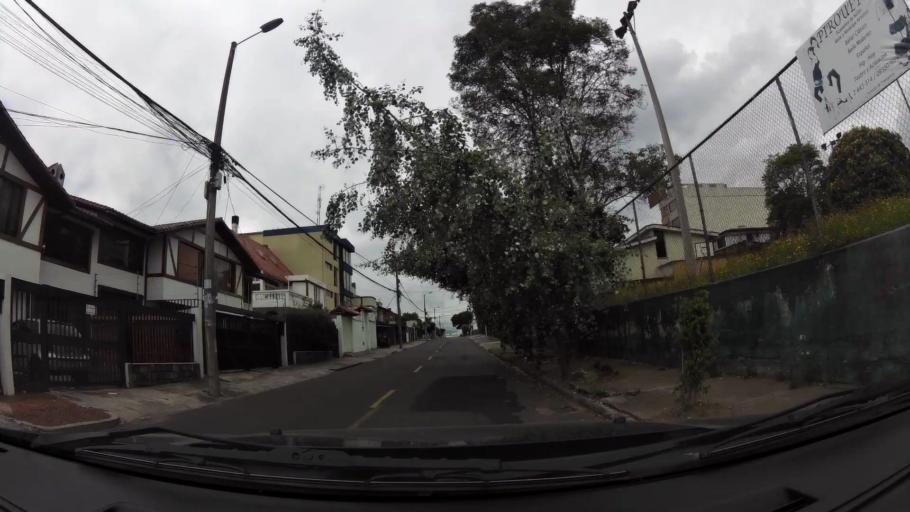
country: EC
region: Pichincha
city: Quito
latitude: -0.1810
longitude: -78.4961
